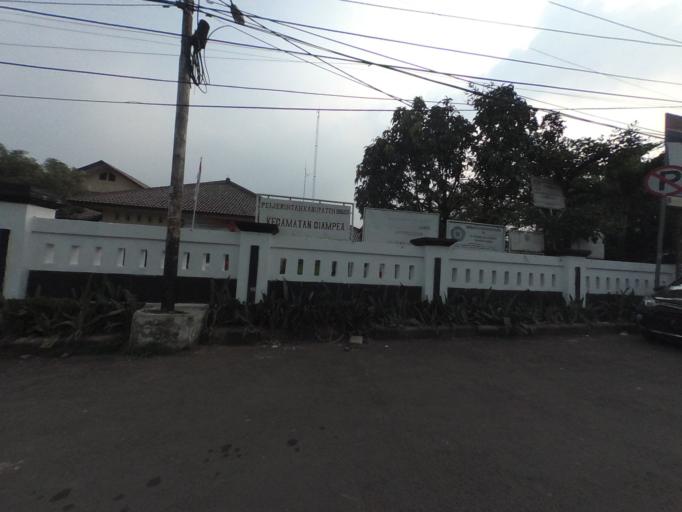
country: ID
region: West Java
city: Ciampea
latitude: -6.5546
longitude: 106.6973
